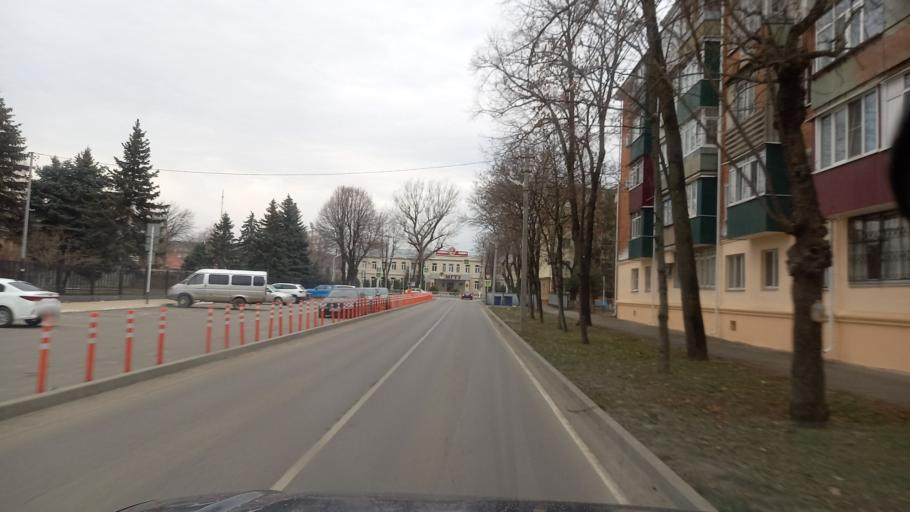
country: RU
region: Adygeya
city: Maykop
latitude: 44.6021
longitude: 40.1058
